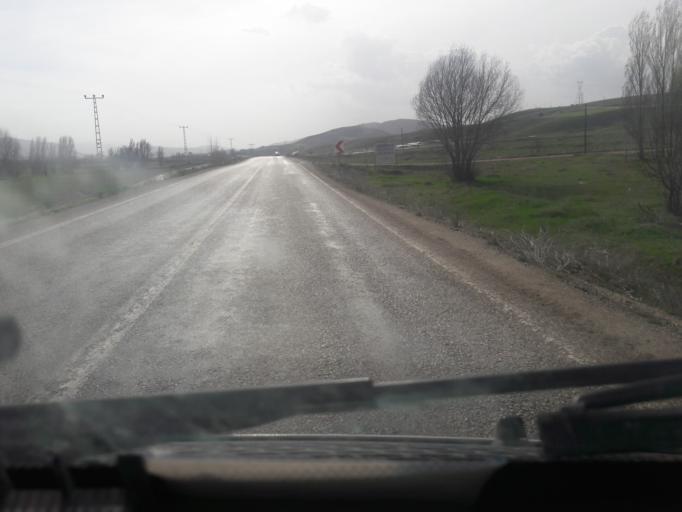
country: TR
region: Gumushane
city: Kelkit
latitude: 40.1435
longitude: 39.4110
